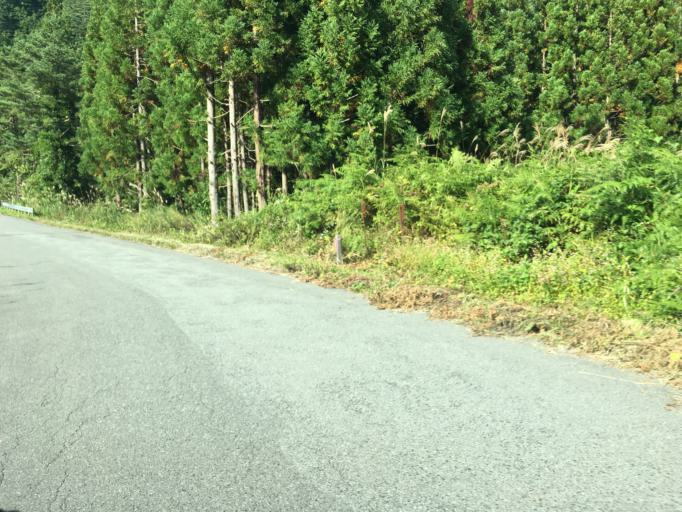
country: JP
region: Yamagata
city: Yonezawa
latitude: 37.8468
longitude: 140.1898
